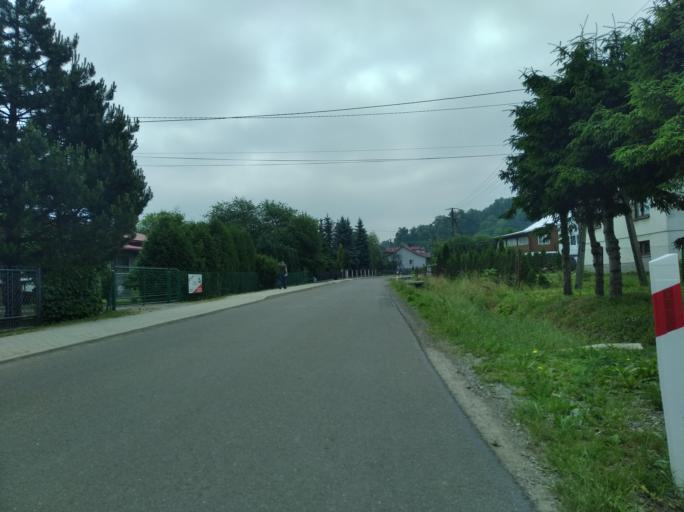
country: PL
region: Subcarpathian Voivodeship
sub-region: Powiat sanocki
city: Besko
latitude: 49.5900
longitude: 21.9448
